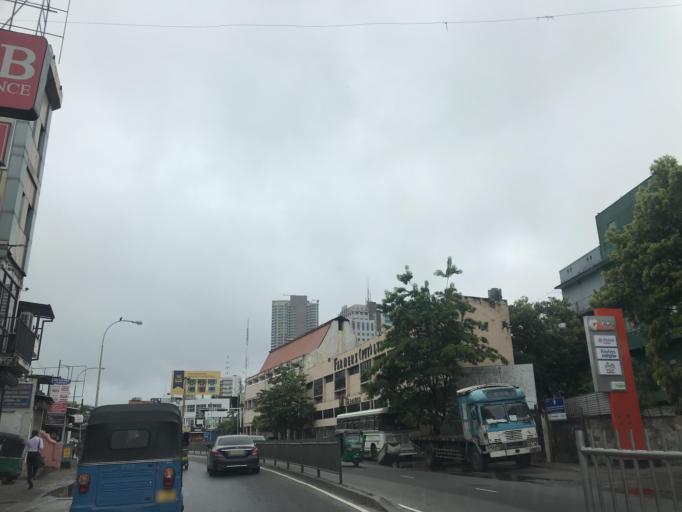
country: LK
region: Western
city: Colombo
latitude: 6.9242
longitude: 79.8649
